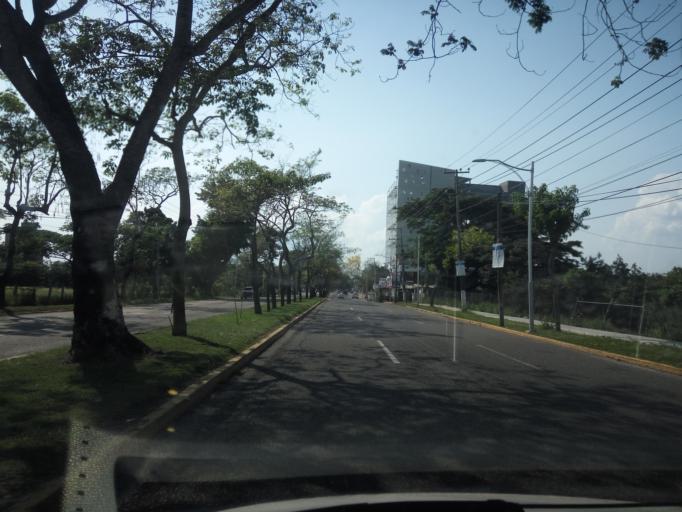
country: MX
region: Tabasco
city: Villahermosa
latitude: 17.9948
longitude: -92.9481
